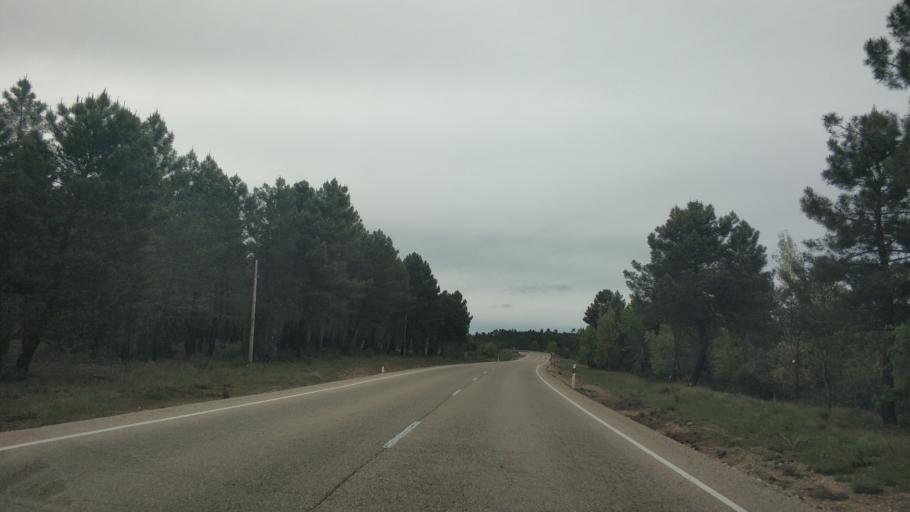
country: ES
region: Castille and Leon
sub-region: Provincia de Soria
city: Bayubas de Abajo
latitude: 41.5160
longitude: -2.9283
